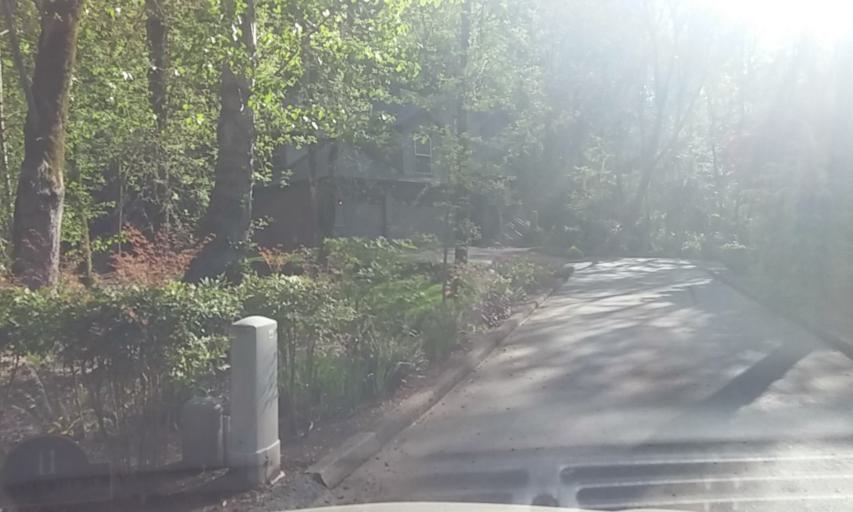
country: US
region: Oregon
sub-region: Washington County
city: Metzger
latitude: 45.4340
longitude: -122.7324
